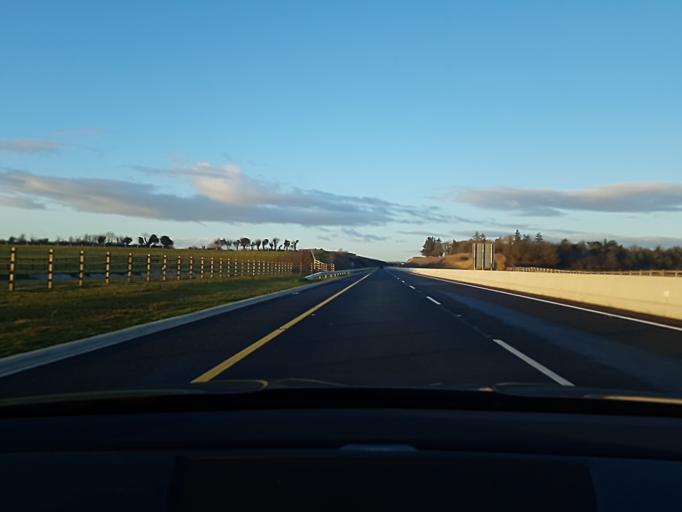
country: IE
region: Connaught
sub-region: County Galway
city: Athenry
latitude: 53.3401
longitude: -8.8020
